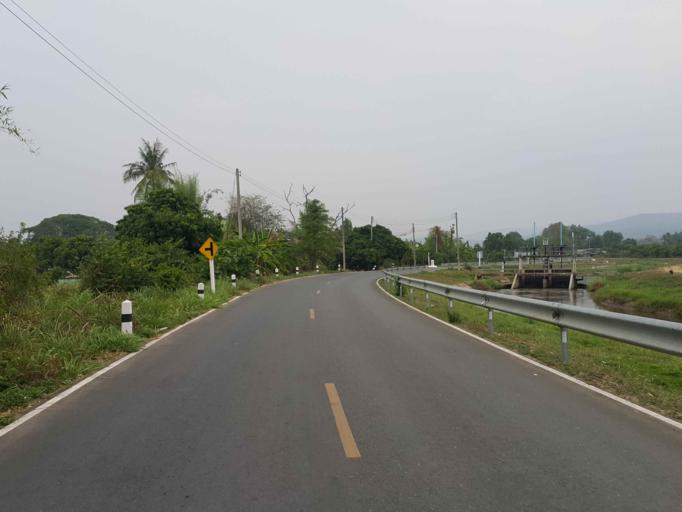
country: TH
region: Chiang Mai
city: Mae Taeng
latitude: 18.9910
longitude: 98.9794
